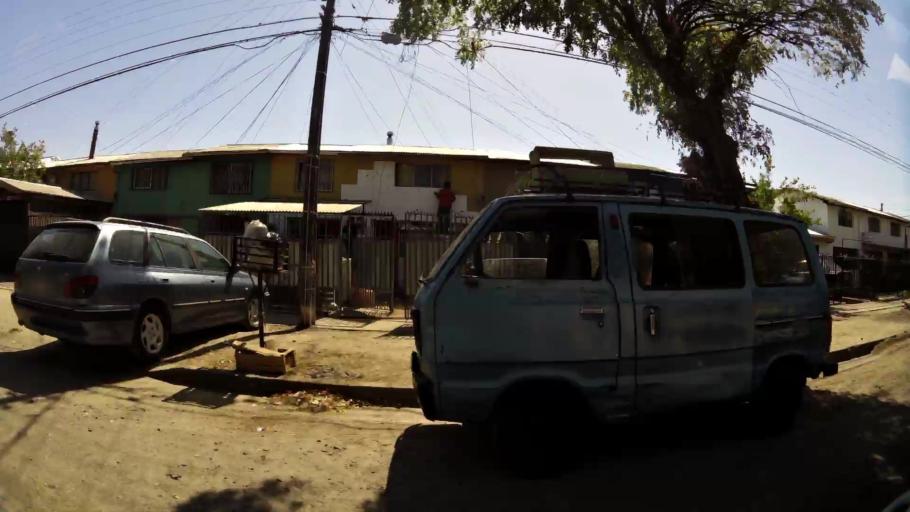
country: CL
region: Maule
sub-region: Provincia de Talca
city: Talca
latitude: -35.4347
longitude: -71.6606
